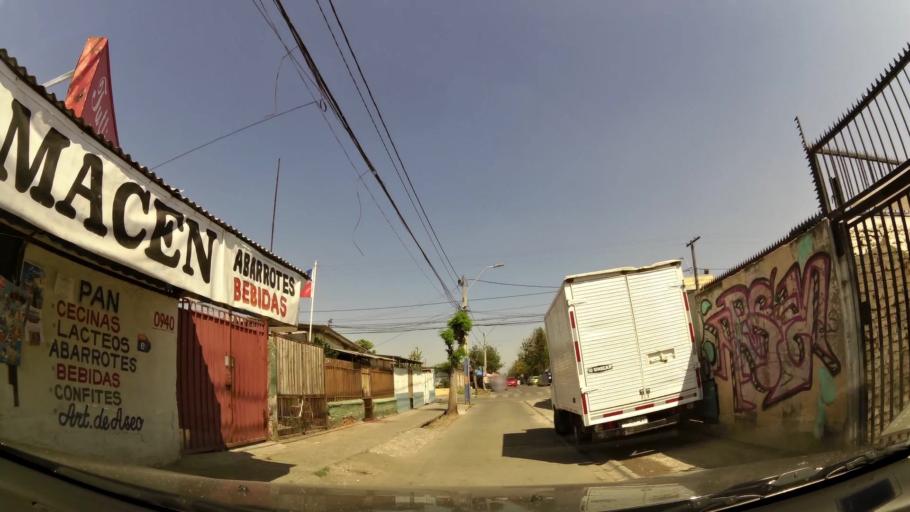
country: CL
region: Santiago Metropolitan
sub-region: Provincia de Maipo
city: San Bernardo
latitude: -33.5753
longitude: -70.7031
